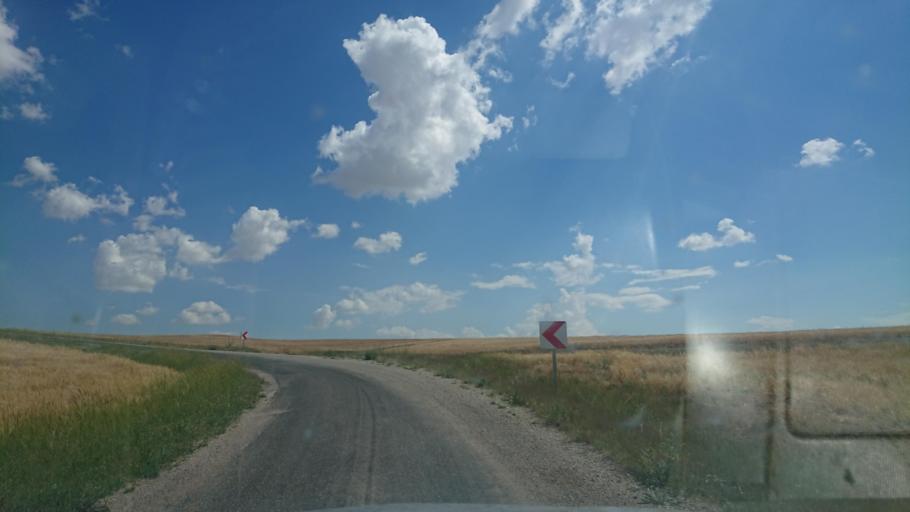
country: TR
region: Aksaray
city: Agacoren
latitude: 38.8082
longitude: 33.7998
